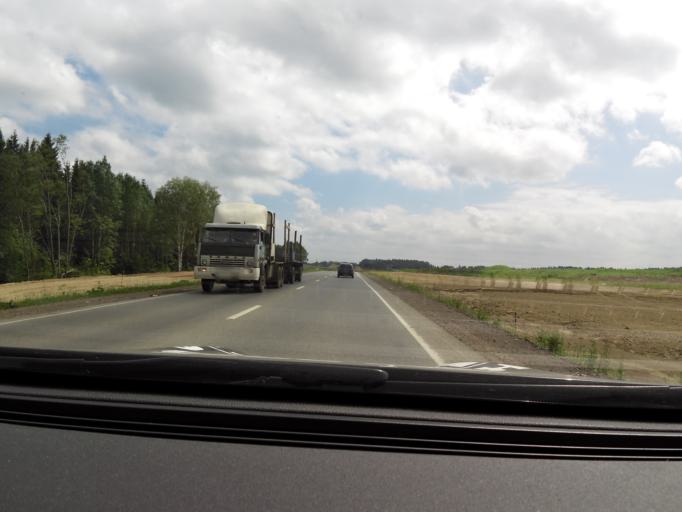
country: RU
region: Perm
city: Bershet'
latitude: 57.6880
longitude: 56.4103
